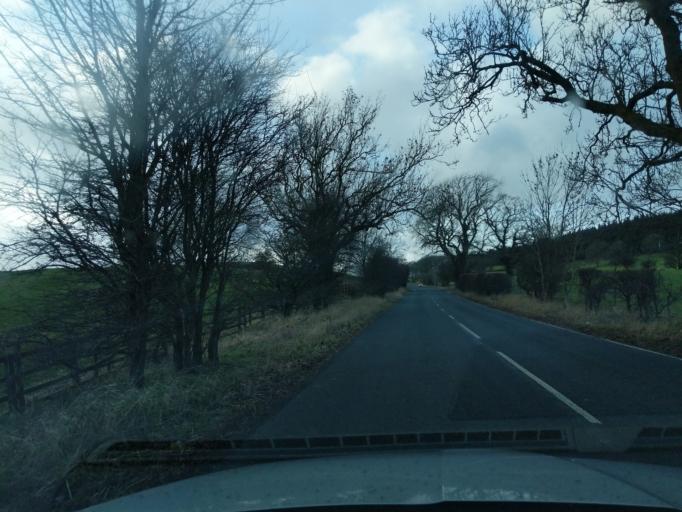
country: GB
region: England
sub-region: North Yorkshire
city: Catterick Garrison
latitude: 54.3464
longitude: -1.7453
